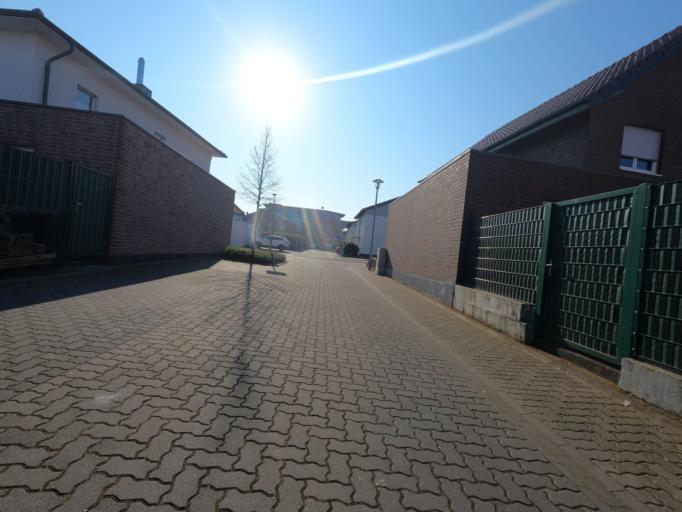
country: DE
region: North Rhine-Westphalia
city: Erkelenz
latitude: 51.0844
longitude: 6.2961
